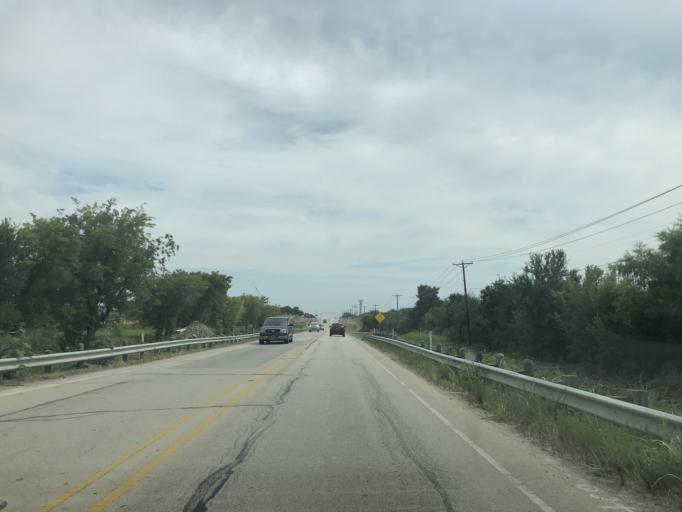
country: US
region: Texas
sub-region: Tarrant County
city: Saginaw
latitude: 32.9061
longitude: -97.3489
